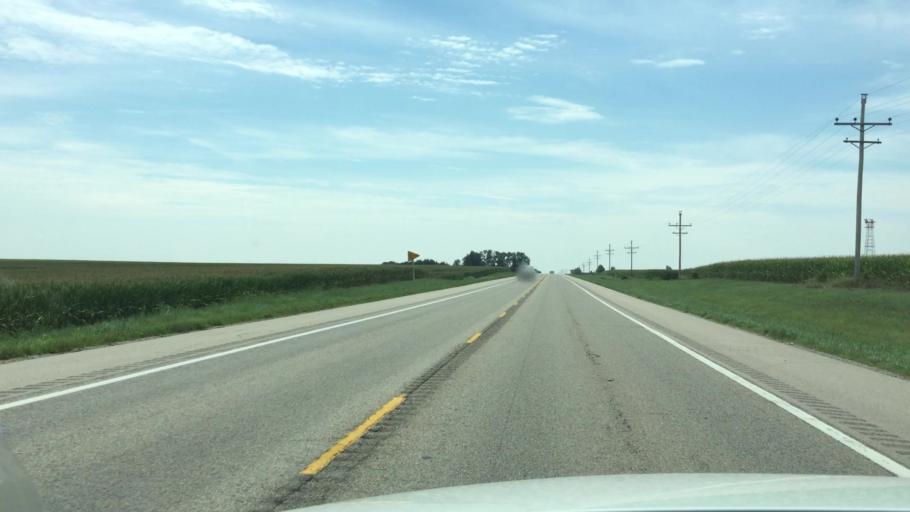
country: US
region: Kansas
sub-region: Nemaha County
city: Sabetha
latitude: 39.7685
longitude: -95.7296
